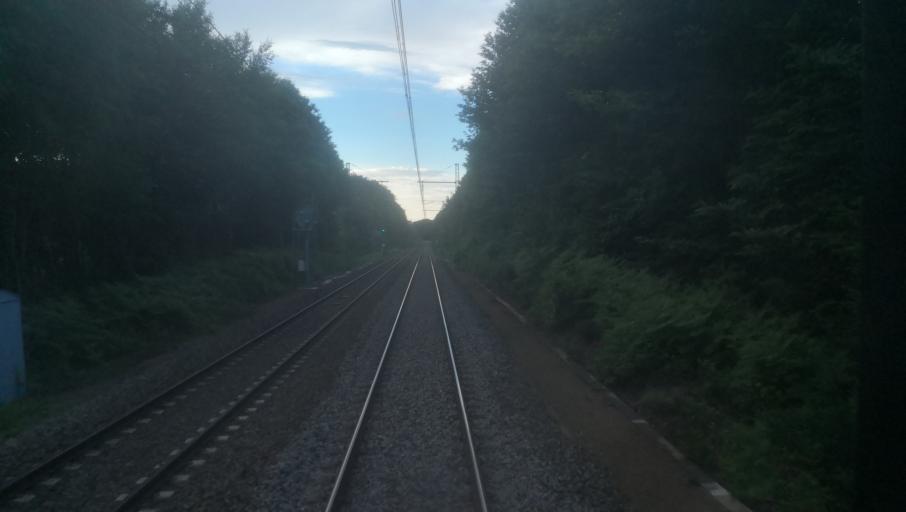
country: FR
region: Limousin
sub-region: Departement de la Creuse
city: La Souterraine
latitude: 46.2665
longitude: 1.4743
